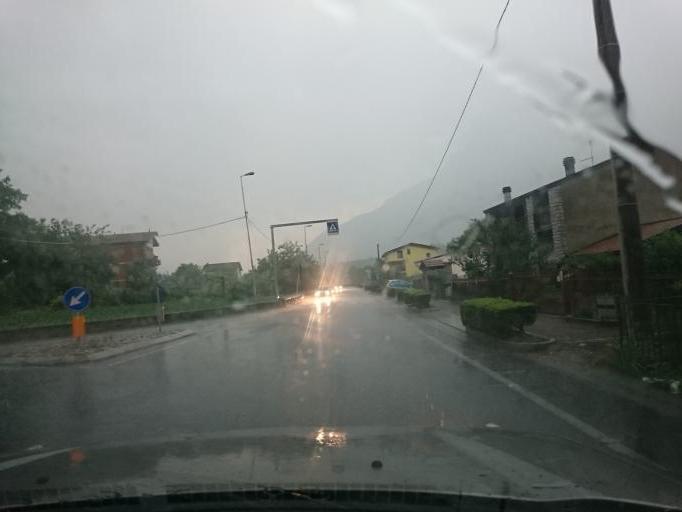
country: IT
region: Lombardy
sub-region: Provincia di Brescia
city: Ceto
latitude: 46.0148
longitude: 10.3474
